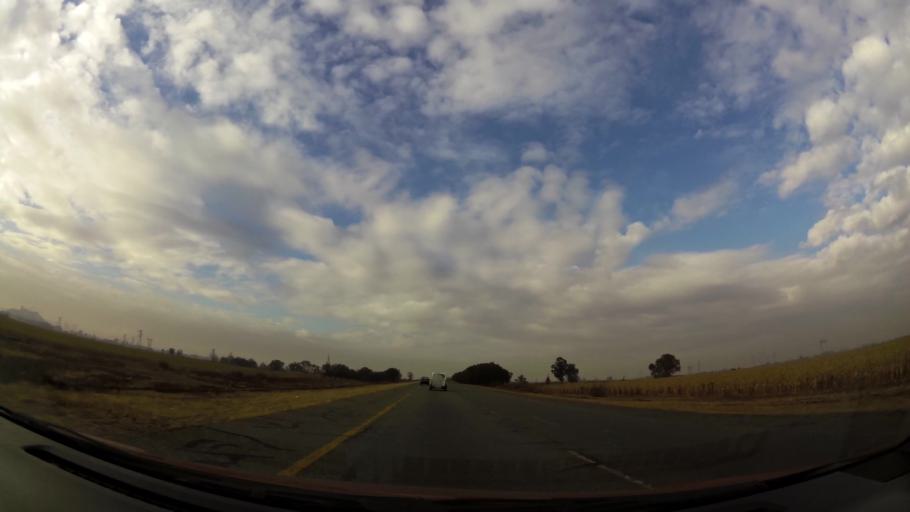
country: ZA
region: Gauteng
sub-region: Sedibeng District Municipality
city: Vanderbijlpark
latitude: -26.6613
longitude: 27.7851
